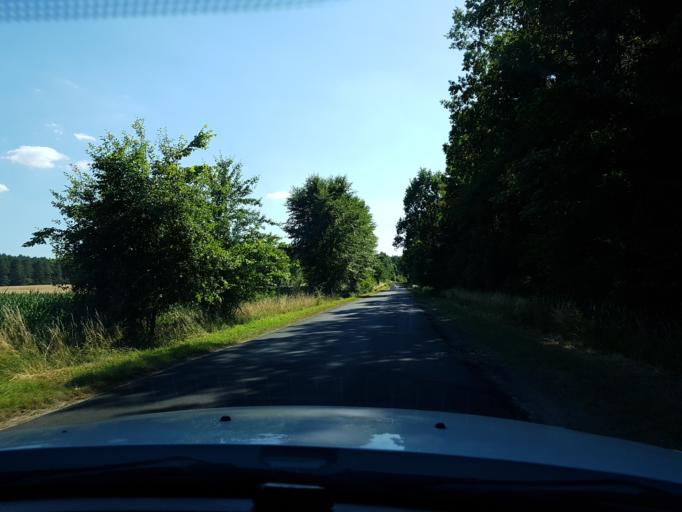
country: PL
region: West Pomeranian Voivodeship
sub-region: Powiat swidwinski
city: Slawoborze
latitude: 53.9311
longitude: 15.8132
